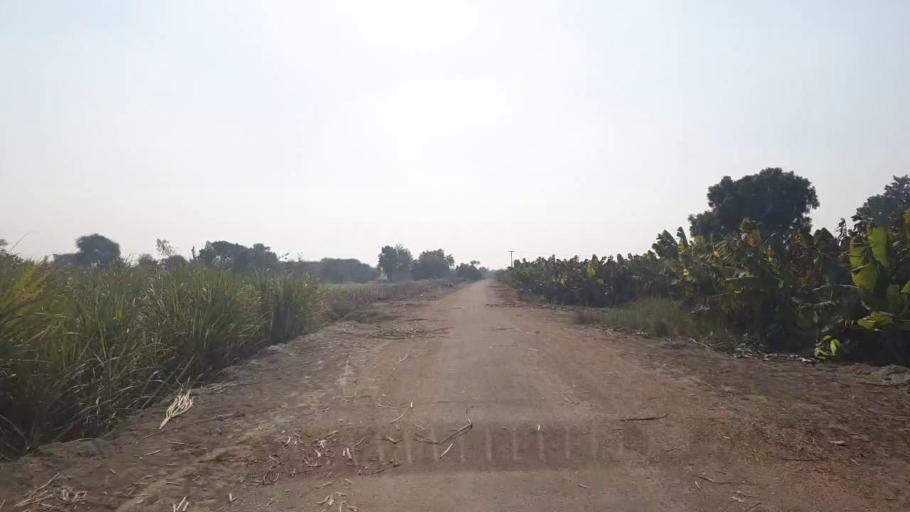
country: PK
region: Sindh
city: Shahdadpur
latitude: 25.9689
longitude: 68.5403
